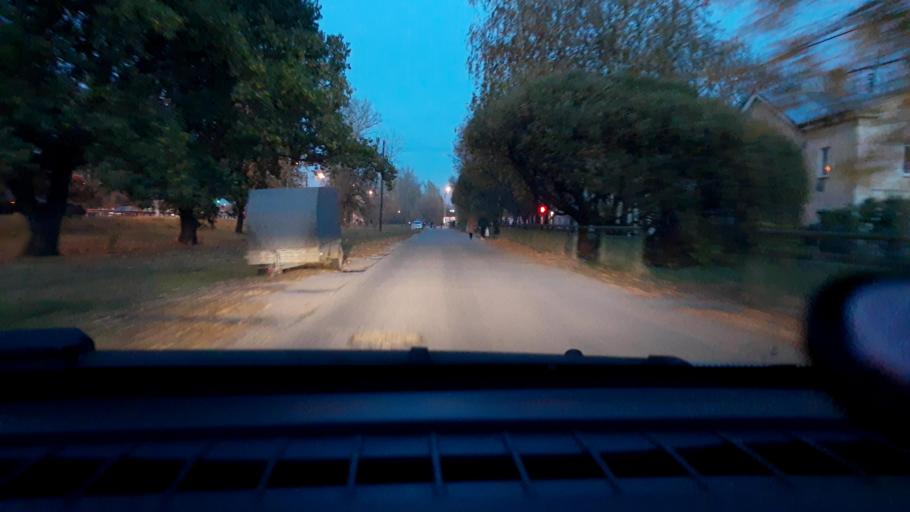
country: RU
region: Nizjnij Novgorod
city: Gorbatovka
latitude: 56.3109
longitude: 43.8104
